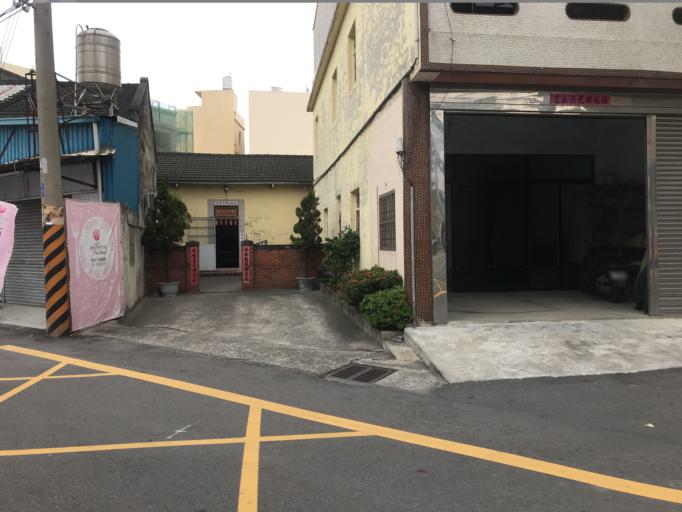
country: TW
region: Taiwan
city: Fengyuan
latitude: 24.3613
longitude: 120.6033
